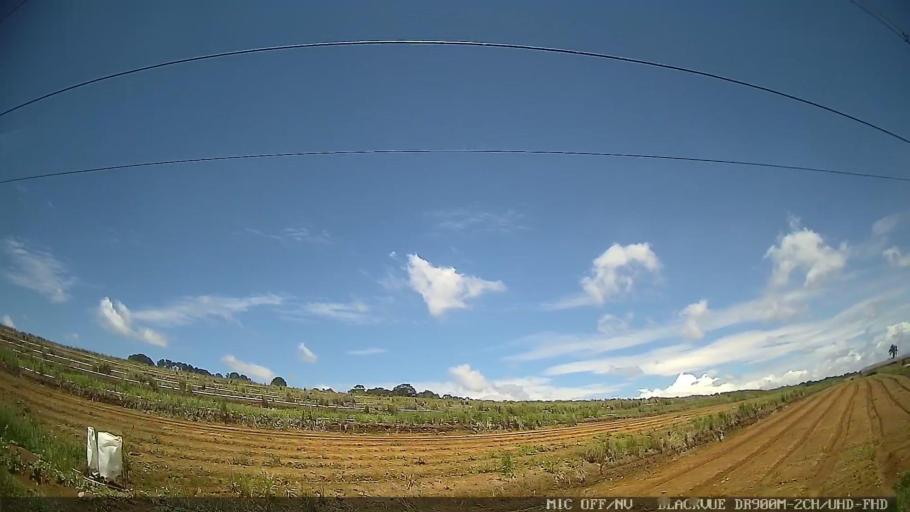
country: BR
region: Sao Paulo
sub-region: Biritiba-Mirim
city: Biritiba Mirim
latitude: -23.5914
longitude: -46.0751
